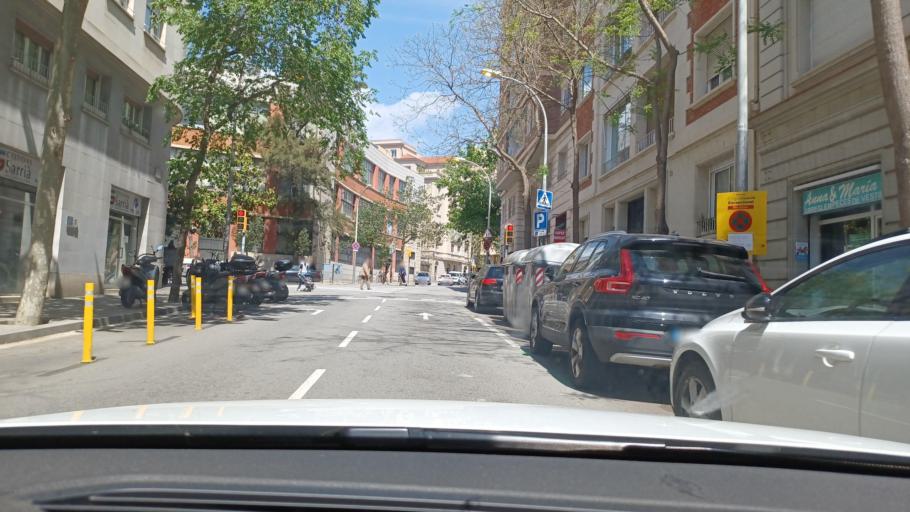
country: ES
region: Catalonia
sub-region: Provincia de Barcelona
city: les Corts
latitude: 41.3945
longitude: 2.1259
